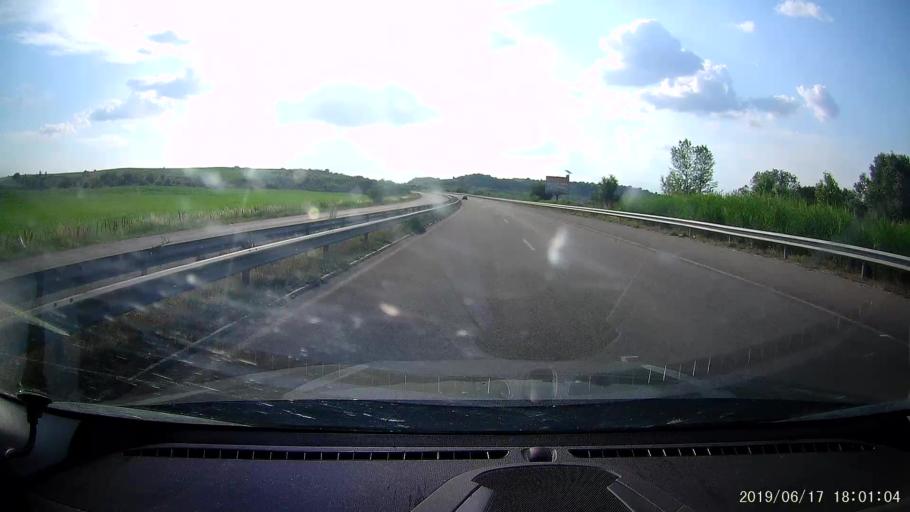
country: BG
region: Khaskovo
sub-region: Obshtina Svilengrad
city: Svilengrad
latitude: 41.7435
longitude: 26.2653
